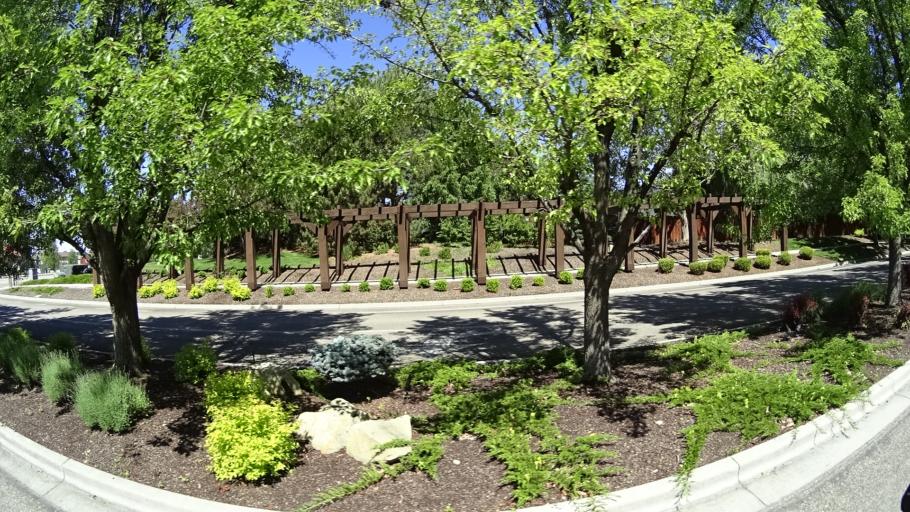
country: US
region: Idaho
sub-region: Ada County
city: Boise
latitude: 43.5694
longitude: -116.1204
